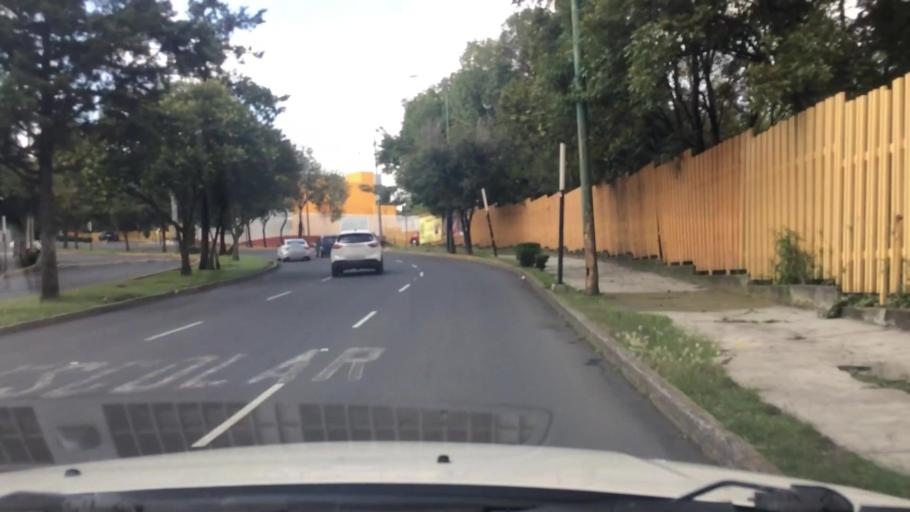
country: MX
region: Mexico City
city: Alvaro Obregon
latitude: 19.3541
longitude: -99.2134
